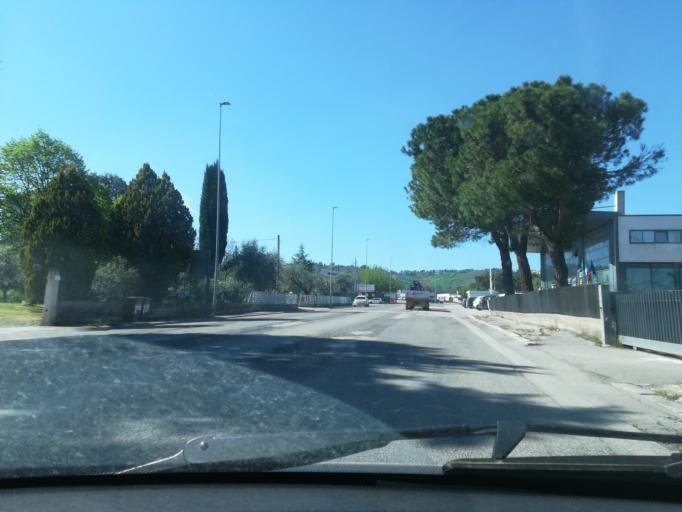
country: IT
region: The Marches
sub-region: Provincia di Macerata
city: Piediripa
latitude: 43.2774
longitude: 13.4919
